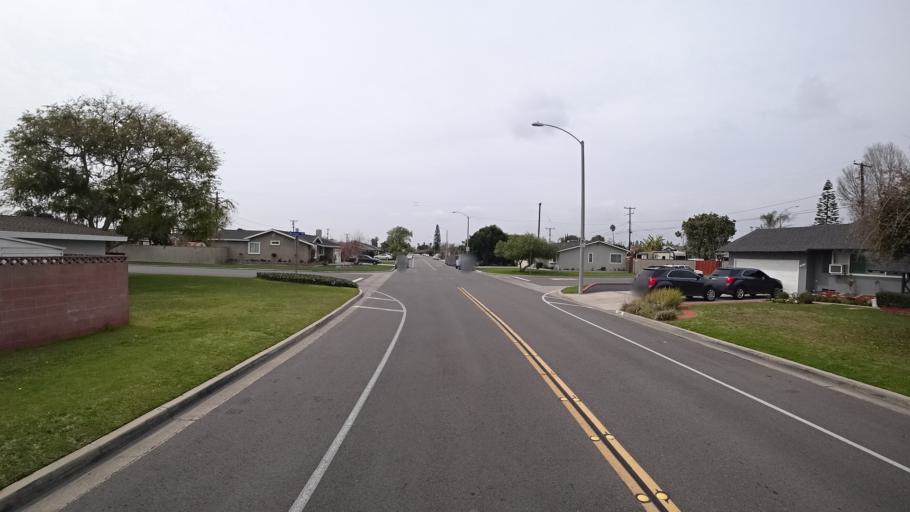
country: US
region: California
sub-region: Orange County
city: Stanton
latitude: 33.8208
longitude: -117.9866
